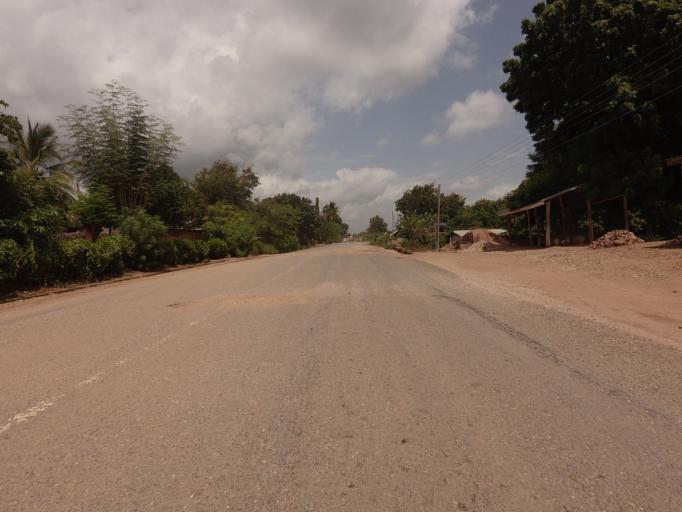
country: GH
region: Volta
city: Ho
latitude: 6.7145
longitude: 0.3372
